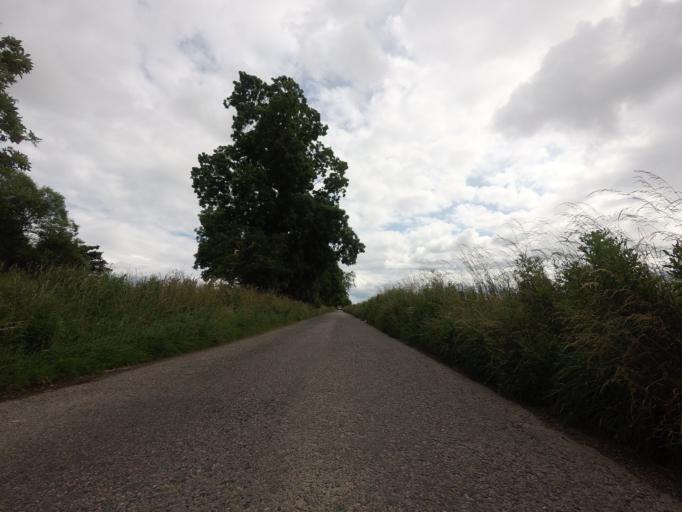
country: GB
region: Scotland
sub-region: Moray
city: Lhanbryd
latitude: 57.6453
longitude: -3.2557
